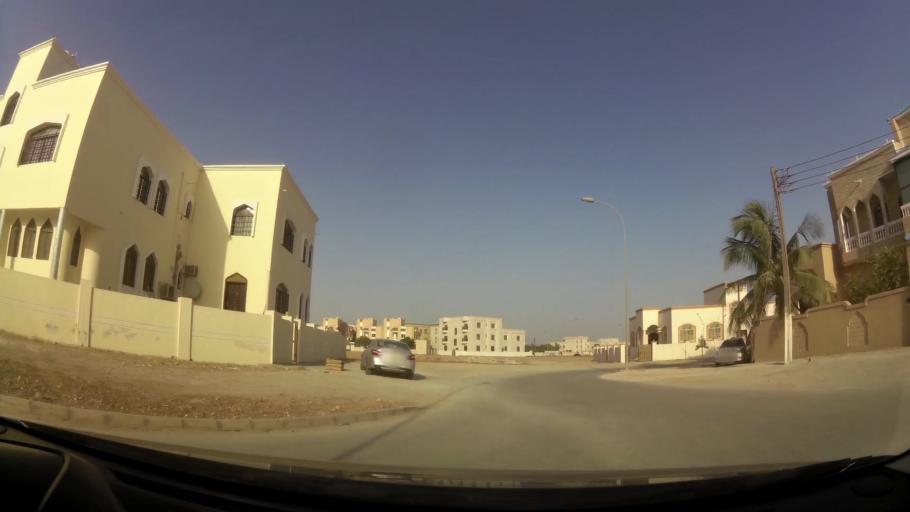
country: OM
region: Zufar
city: Salalah
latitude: 17.0130
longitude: 54.0336
